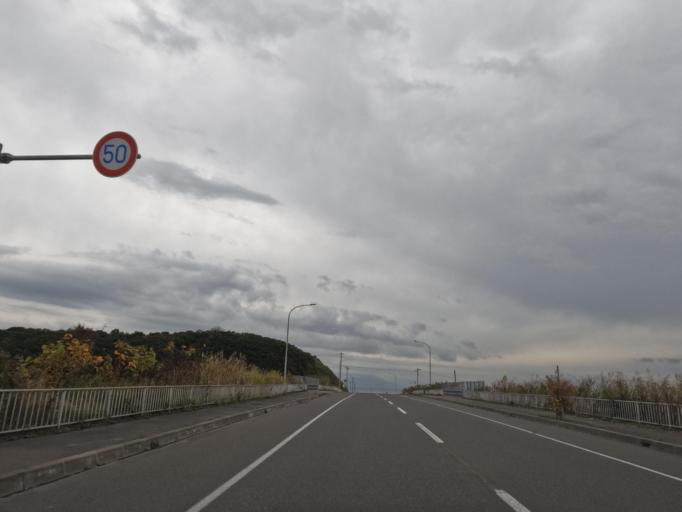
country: JP
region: Hokkaido
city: Date
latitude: 42.3817
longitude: 140.9108
